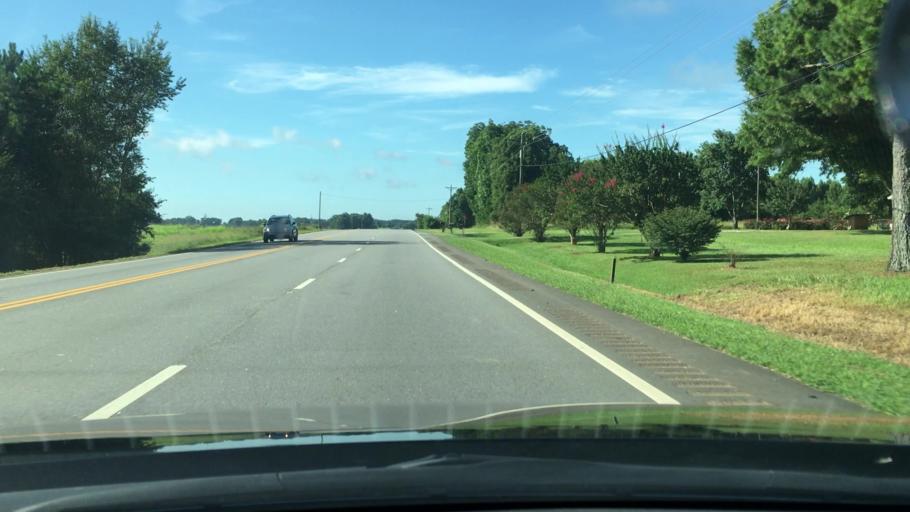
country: US
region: Georgia
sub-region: Morgan County
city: Madison
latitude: 33.4949
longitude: -83.4383
